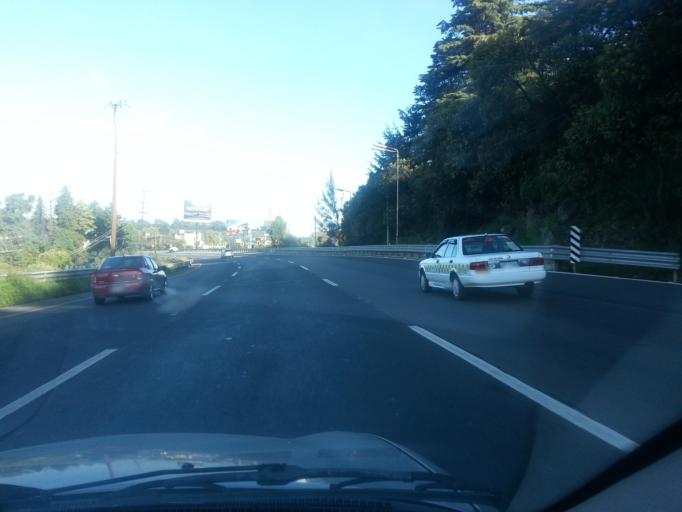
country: MX
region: Mexico
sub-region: Lerma
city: Fraccionamiento y Club de Golf los Encinos
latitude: 19.2841
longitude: -99.4875
